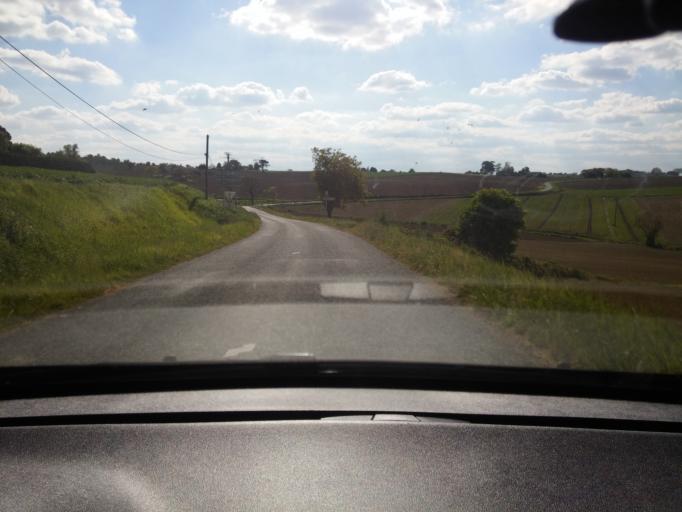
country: FR
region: Aquitaine
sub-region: Departement du Lot-et-Garonne
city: Laplume
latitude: 44.1004
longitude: 0.4390
